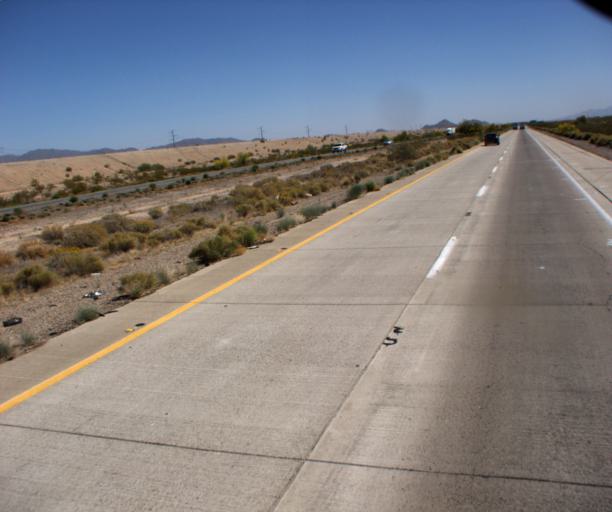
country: US
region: Arizona
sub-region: Maricopa County
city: Buckeye
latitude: 33.4462
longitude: -112.7089
